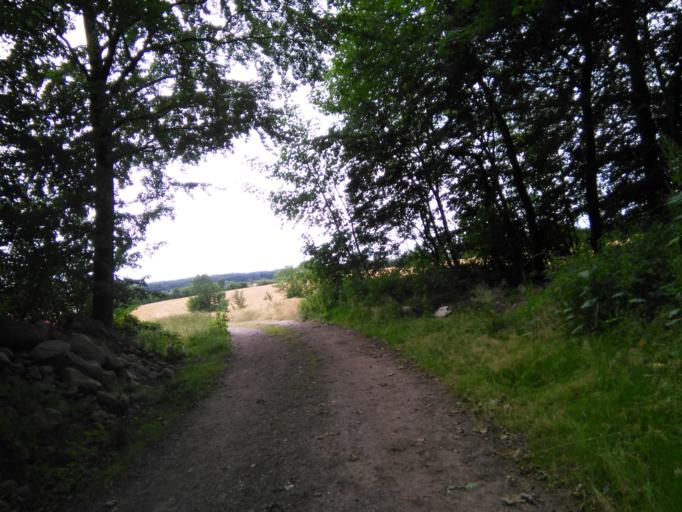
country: DK
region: Central Jutland
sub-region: Arhus Kommune
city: Solbjerg
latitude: 55.9887
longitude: 10.0797
